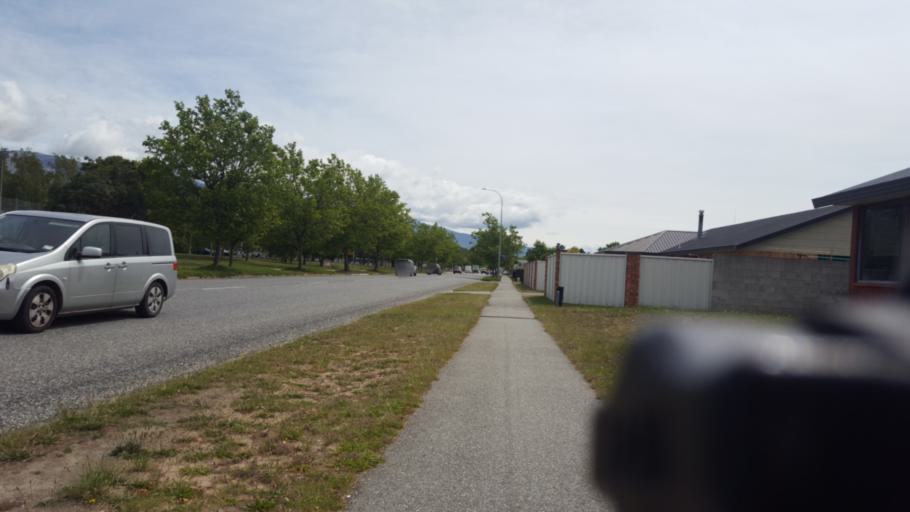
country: NZ
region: Otago
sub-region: Queenstown-Lakes District
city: Wanaka
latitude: -45.0427
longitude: 169.1969
